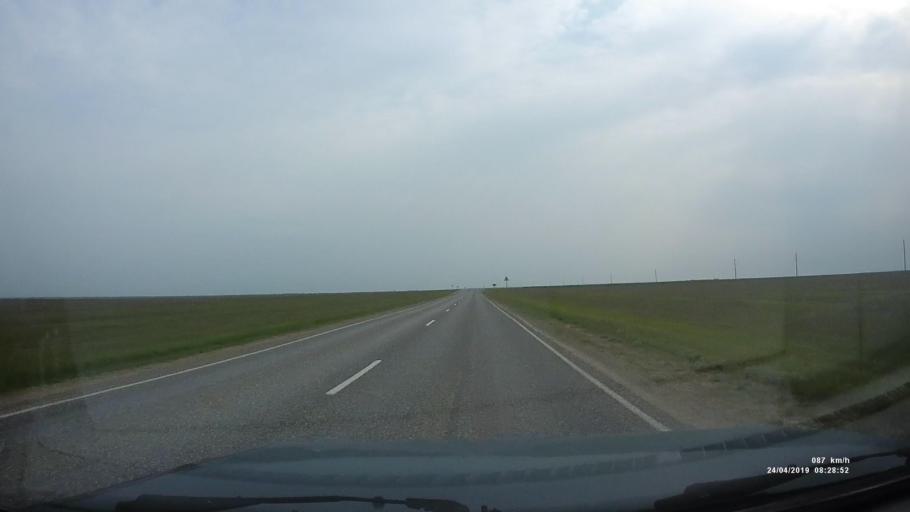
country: RU
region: Kalmykiya
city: Priyutnoye
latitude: 46.1477
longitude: 43.8221
